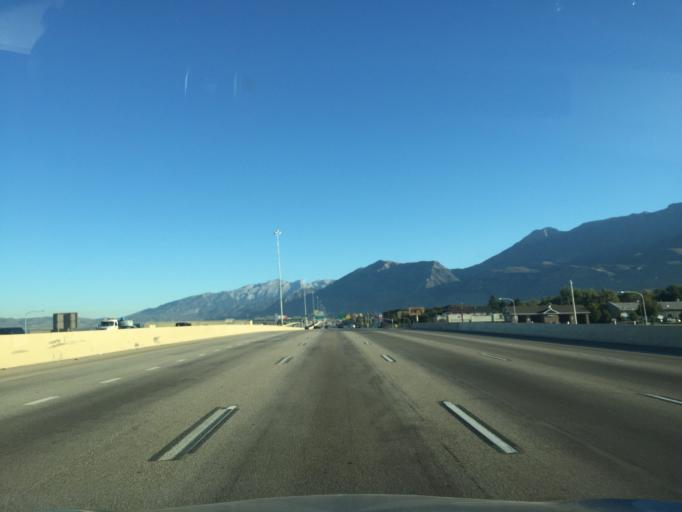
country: US
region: Utah
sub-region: Utah County
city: Orem
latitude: 40.2969
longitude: -111.7256
